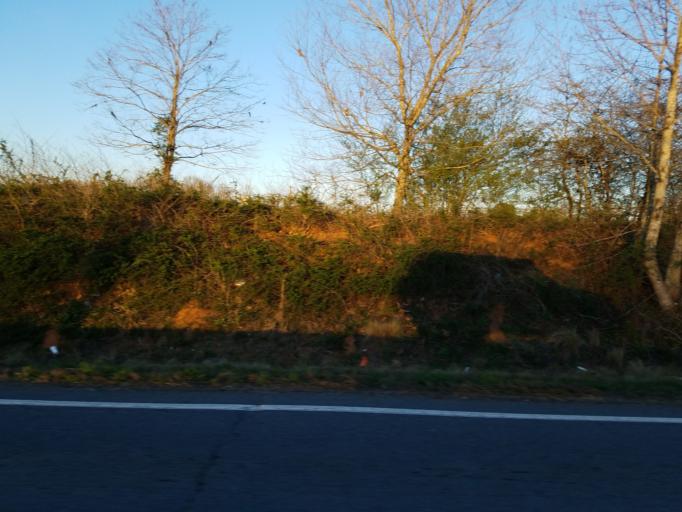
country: US
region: Georgia
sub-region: Dawson County
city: Dawsonville
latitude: 34.3524
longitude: -84.0313
